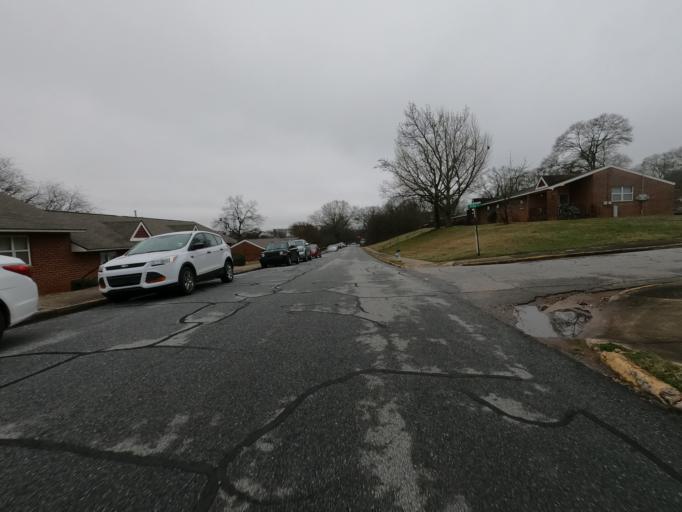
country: US
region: Georgia
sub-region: Clarke County
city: Athens
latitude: 33.9534
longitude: -83.3818
